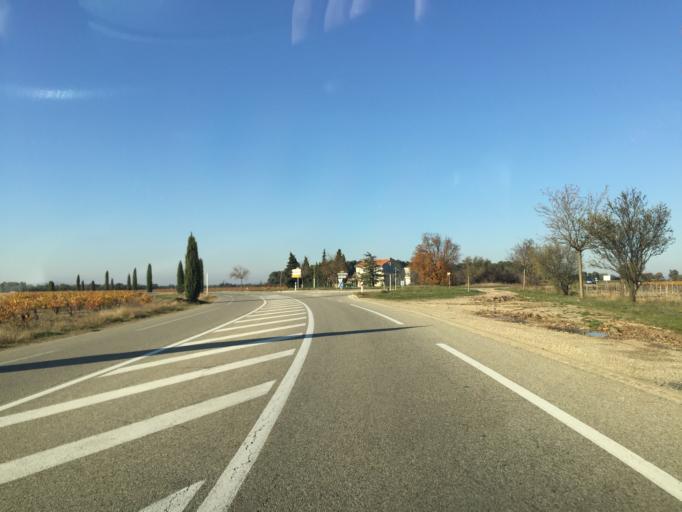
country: FR
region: Provence-Alpes-Cote d'Azur
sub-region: Departement du Vaucluse
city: Sainte-Cecile-les-Vignes
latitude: 44.2378
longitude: 4.9102
